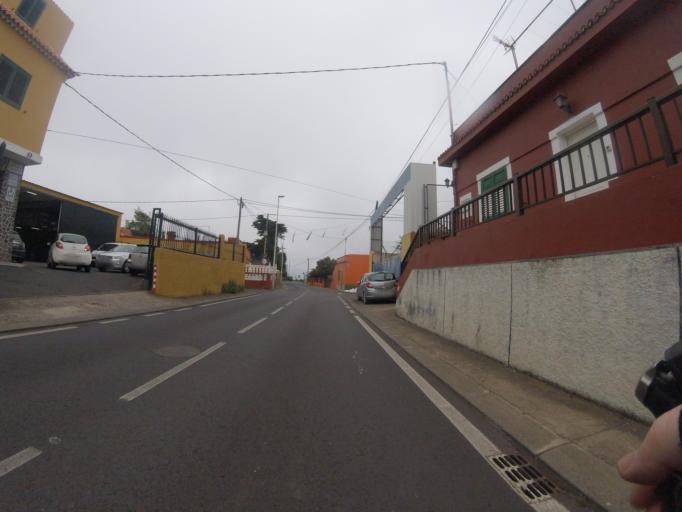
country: ES
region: Canary Islands
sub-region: Provincia de Santa Cruz de Tenerife
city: Tacoronte
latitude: 28.4966
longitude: -16.3786
